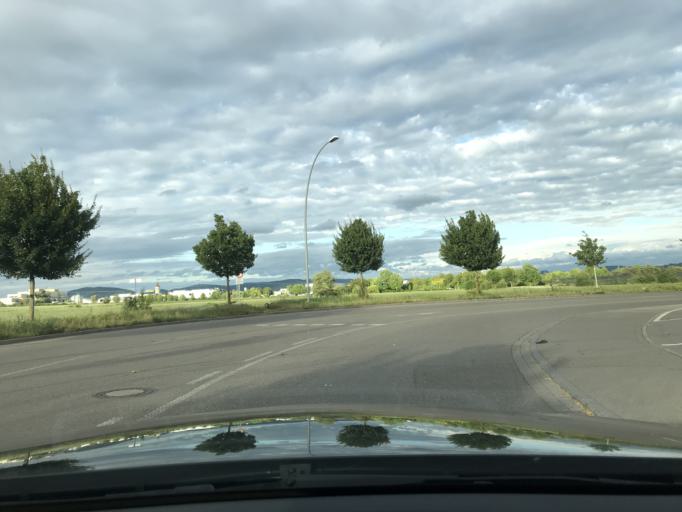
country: DE
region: Baden-Wuerttemberg
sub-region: Regierungsbezirk Stuttgart
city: Fellbach
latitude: 48.8180
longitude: 9.2852
